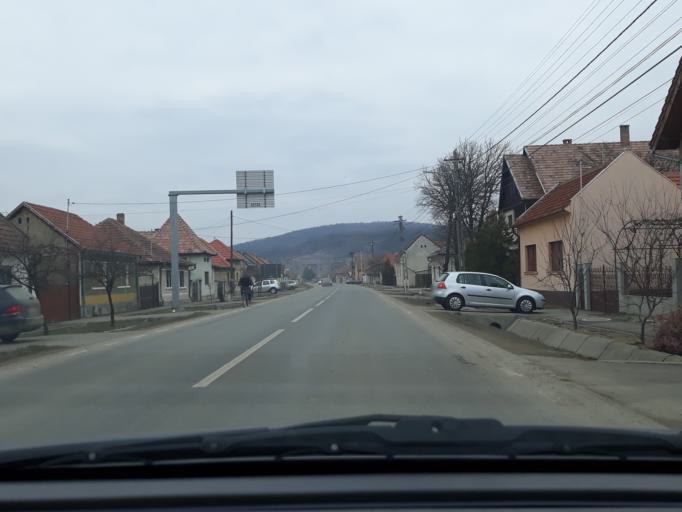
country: RO
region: Salaj
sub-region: Comuna Nusfalau
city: Nusfalau
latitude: 47.2009
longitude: 22.7118
